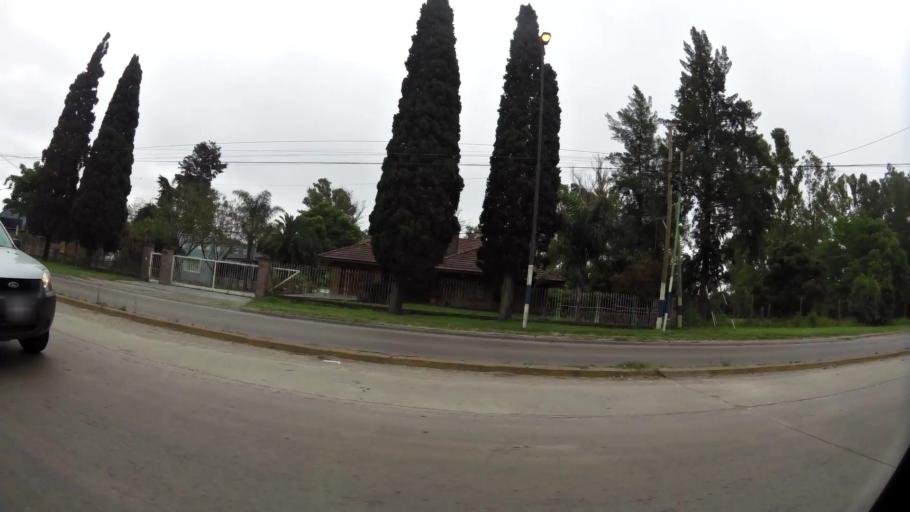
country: AR
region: Buenos Aires
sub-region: Partido de La Plata
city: La Plata
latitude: -34.9651
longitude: -58.0149
